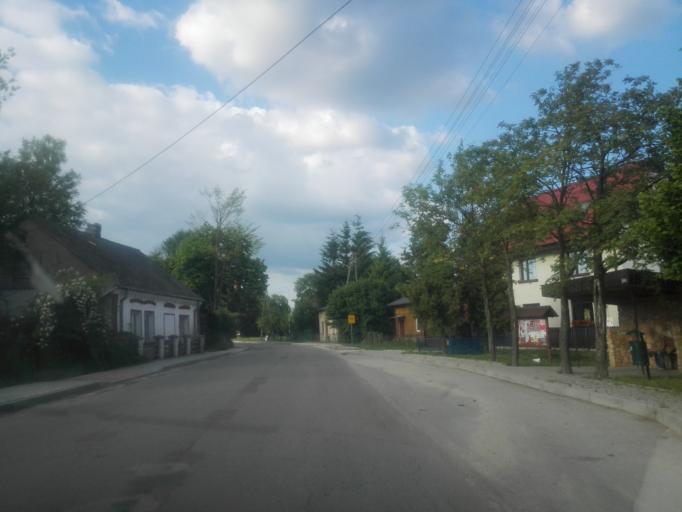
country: PL
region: Swietokrzyskie
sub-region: Powiat jedrzejowski
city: Slupia
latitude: 50.7020
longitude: 19.9488
